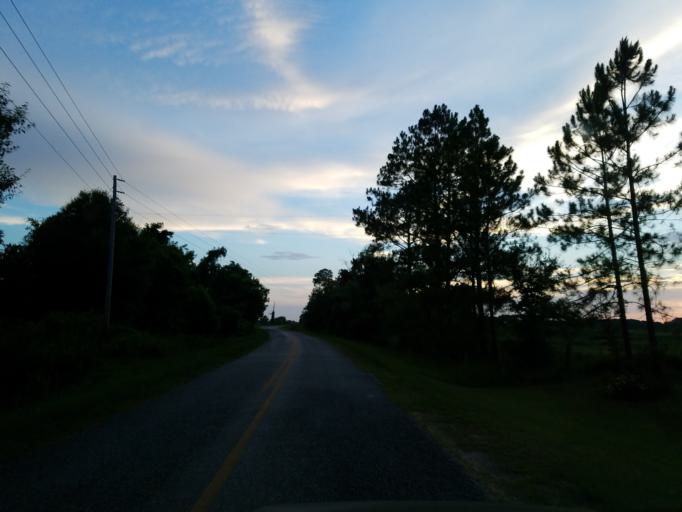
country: US
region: Georgia
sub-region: Crisp County
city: Cordele
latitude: 31.8355
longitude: -83.7682
